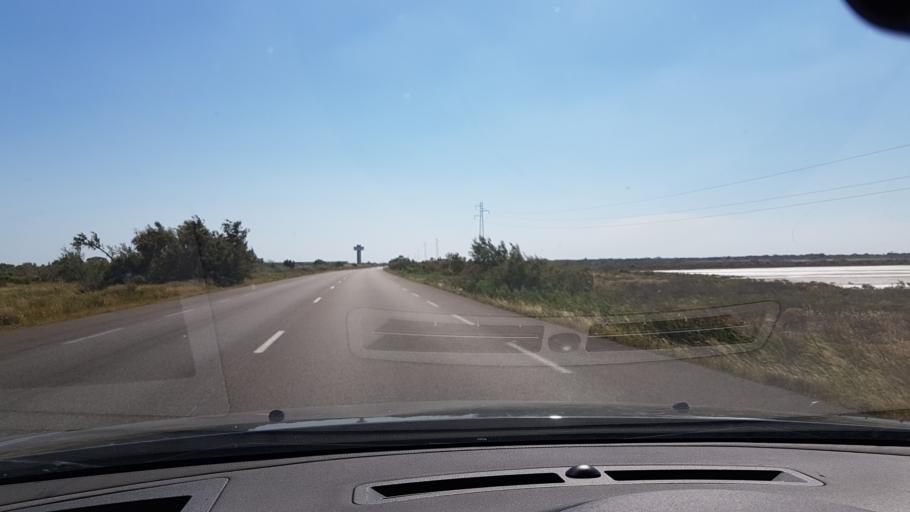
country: FR
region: Provence-Alpes-Cote d'Azur
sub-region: Departement des Bouches-du-Rhone
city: Port-Saint-Louis-du-Rhone
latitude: 43.4291
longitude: 4.8225
